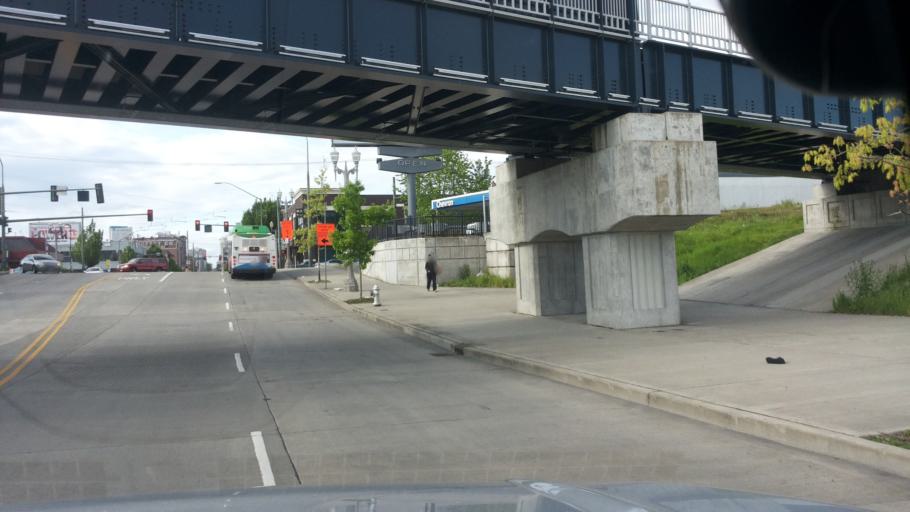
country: US
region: Washington
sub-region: Pierce County
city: Tacoma
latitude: 47.2382
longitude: -122.4352
